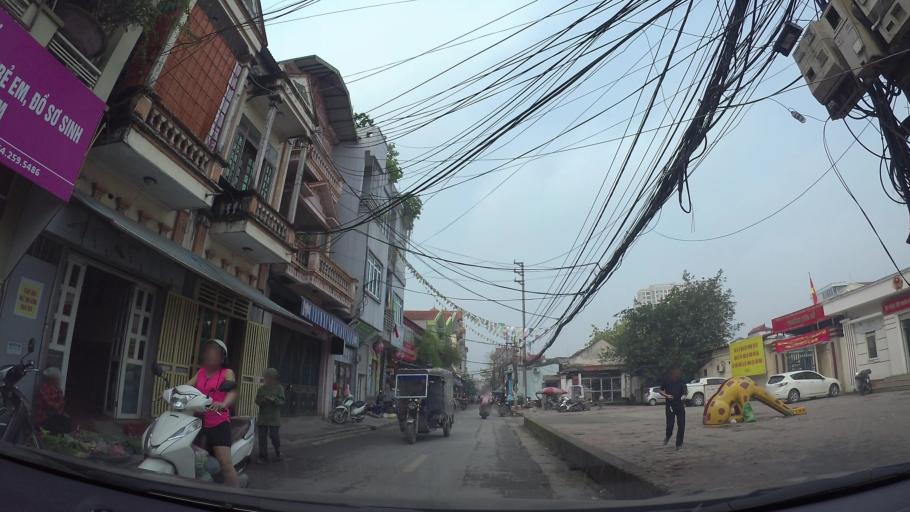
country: VN
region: Ha Noi
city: Van Dien
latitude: 20.9677
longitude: 105.8717
